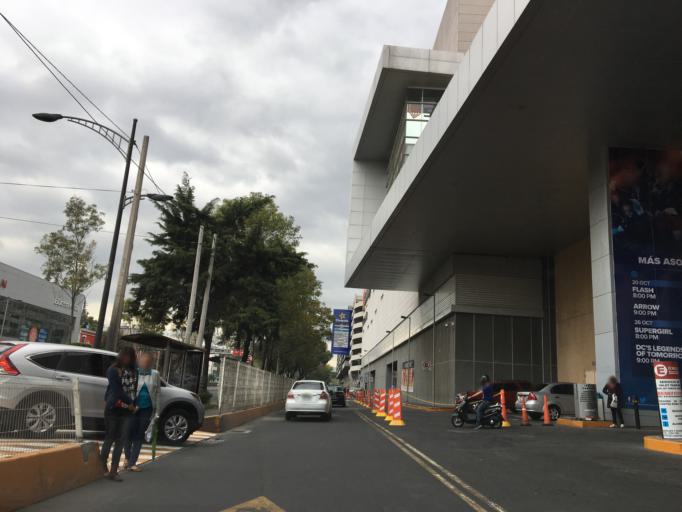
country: MX
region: Mexico City
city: Cuauhtemoc
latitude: 19.4479
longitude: -99.1527
